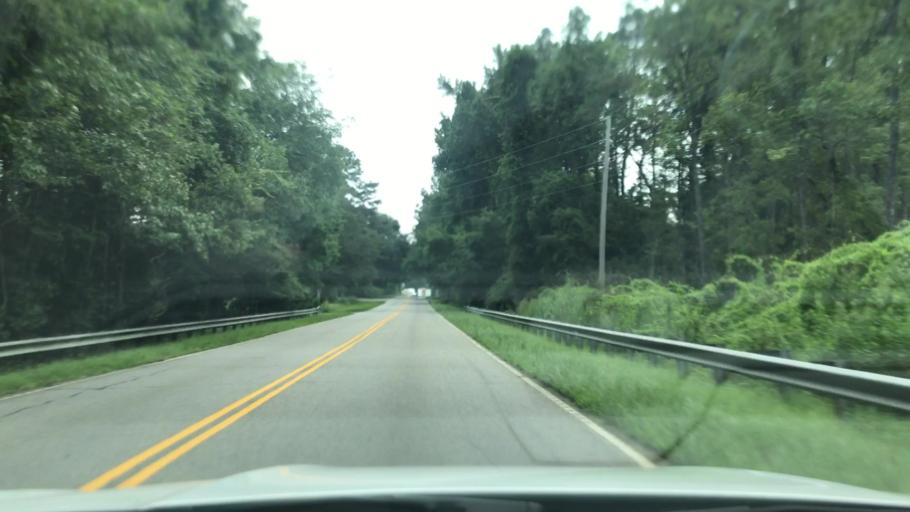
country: US
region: South Carolina
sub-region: Georgetown County
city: Murrells Inlet
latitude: 33.5584
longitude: -79.2153
